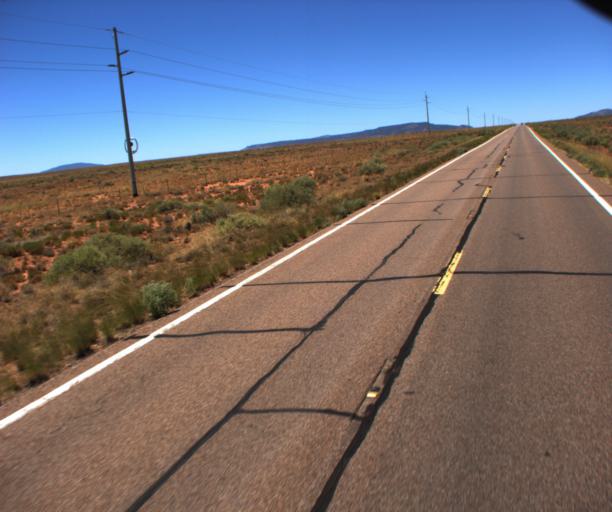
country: US
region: Arizona
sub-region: Coconino County
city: LeChee
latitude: 34.9515
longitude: -110.7605
